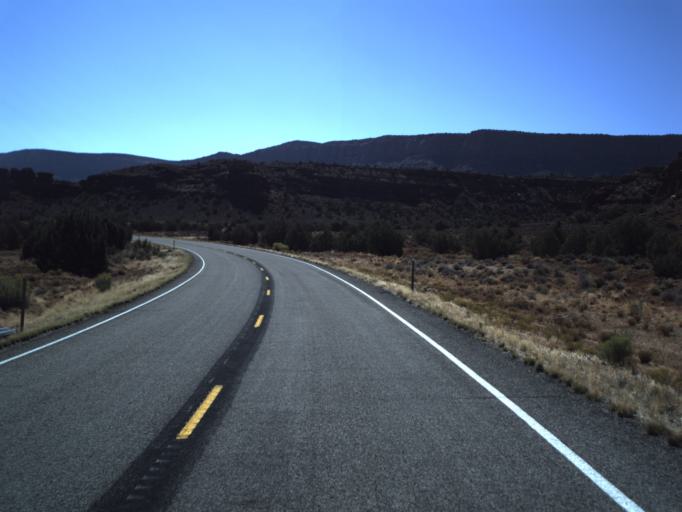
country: US
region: Utah
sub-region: San Juan County
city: Blanding
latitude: 37.7081
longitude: -110.2421
